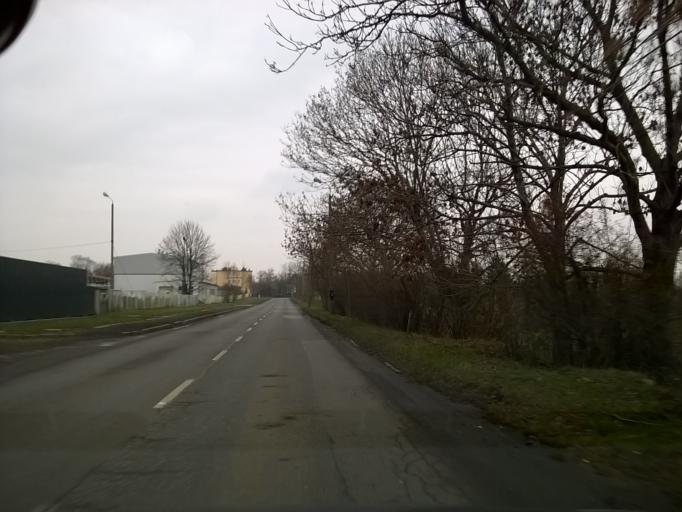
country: PL
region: Silesian Voivodeship
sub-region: Chorzow
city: Chorzow
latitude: 50.3213
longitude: 18.9832
